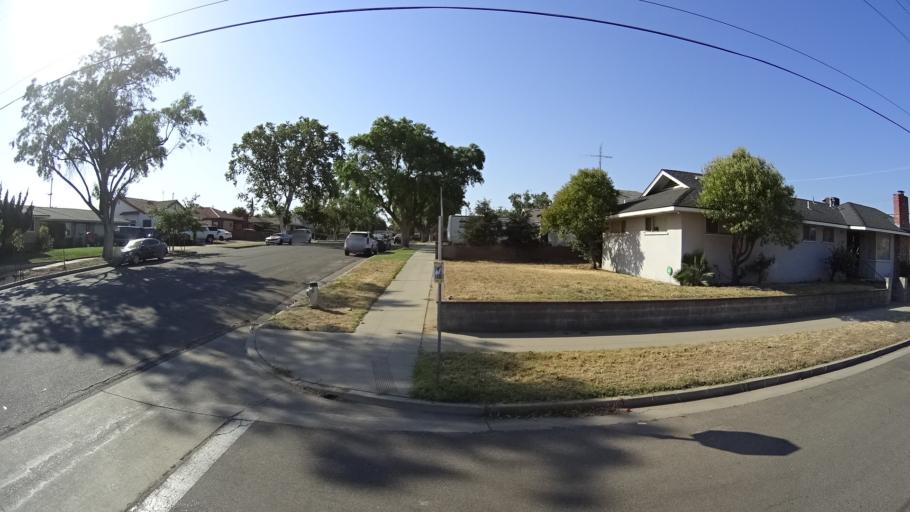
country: US
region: California
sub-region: Fresno County
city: Fresno
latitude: 36.7226
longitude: -119.8084
